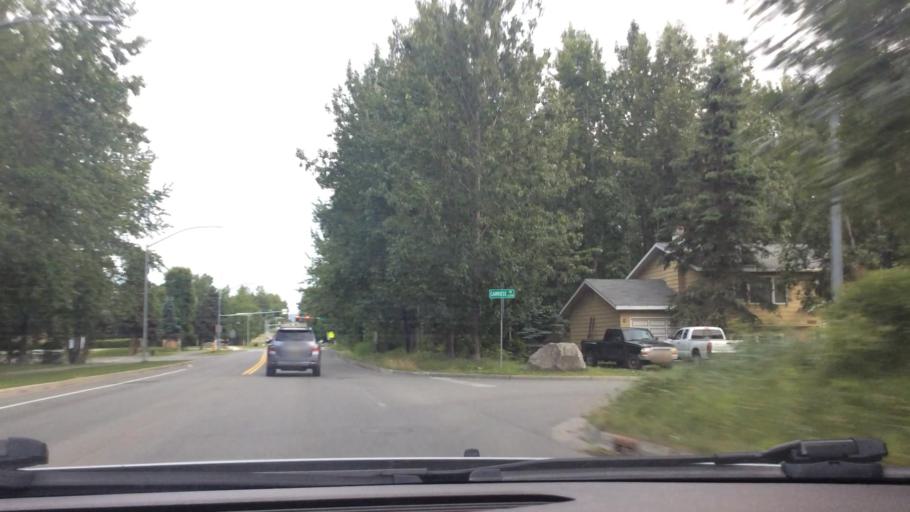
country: US
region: Alaska
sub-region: Anchorage Municipality
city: Anchorage
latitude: 61.1970
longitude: -149.7635
